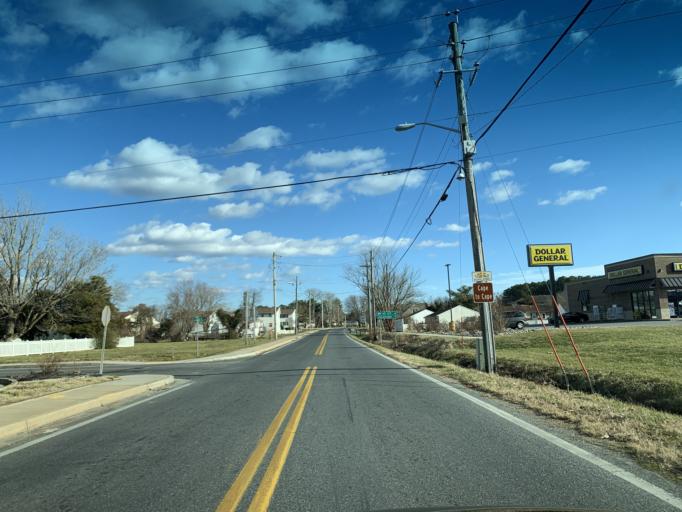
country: US
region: Maryland
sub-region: Worcester County
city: Berlin
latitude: 38.3239
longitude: -75.2109
